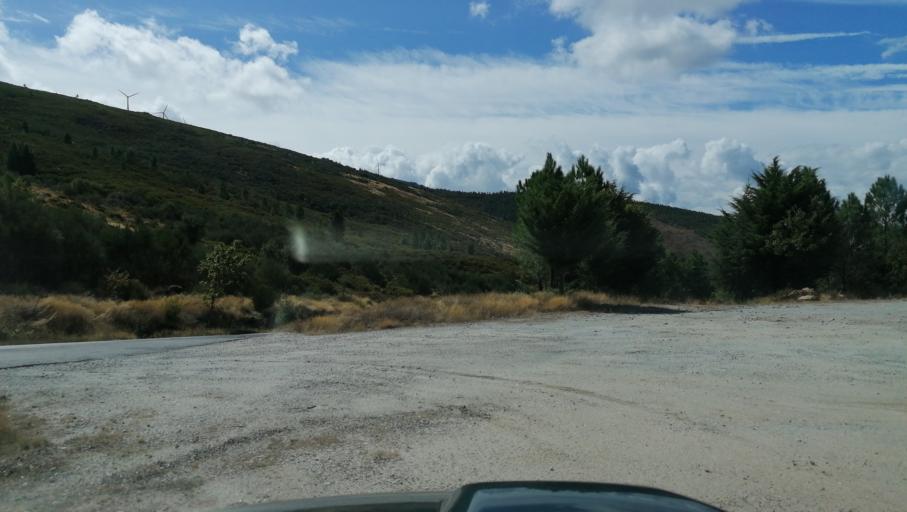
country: PT
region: Vila Real
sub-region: Vila Pouca de Aguiar
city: Vila Pouca de Aguiar
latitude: 41.5560
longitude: -7.7054
